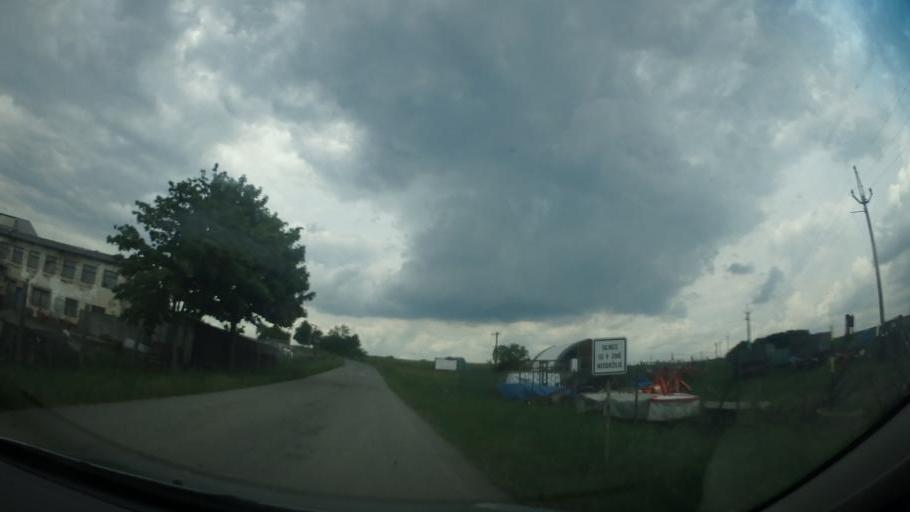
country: CZ
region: South Moravian
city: Olesnice
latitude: 49.4875
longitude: 16.4210
